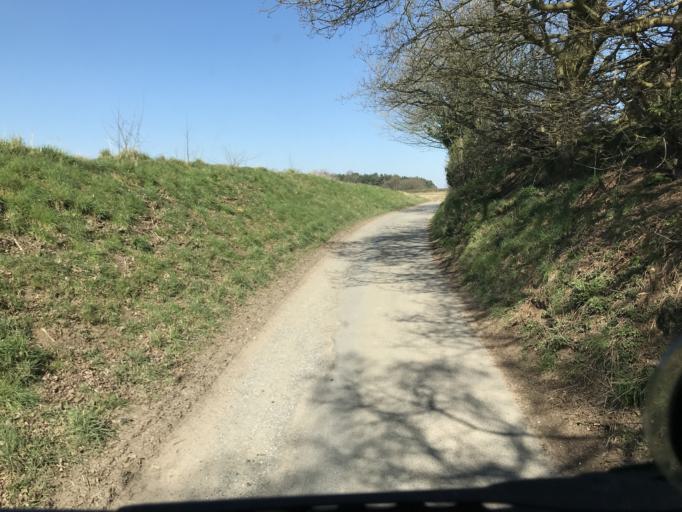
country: GB
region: England
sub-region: Cheshire East
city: Siddington
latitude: 53.2632
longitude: -2.2562
